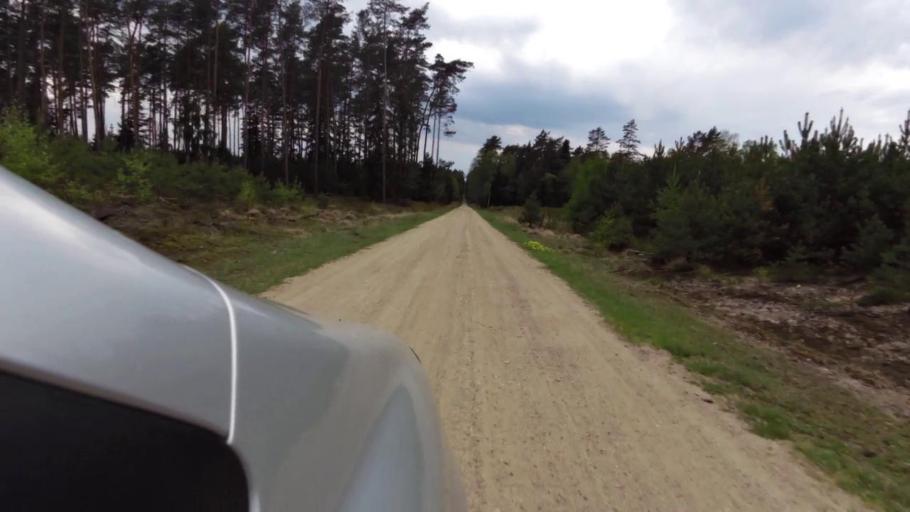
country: PL
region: West Pomeranian Voivodeship
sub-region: Powiat walecki
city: Walcz
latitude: 53.2715
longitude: 16.3673
